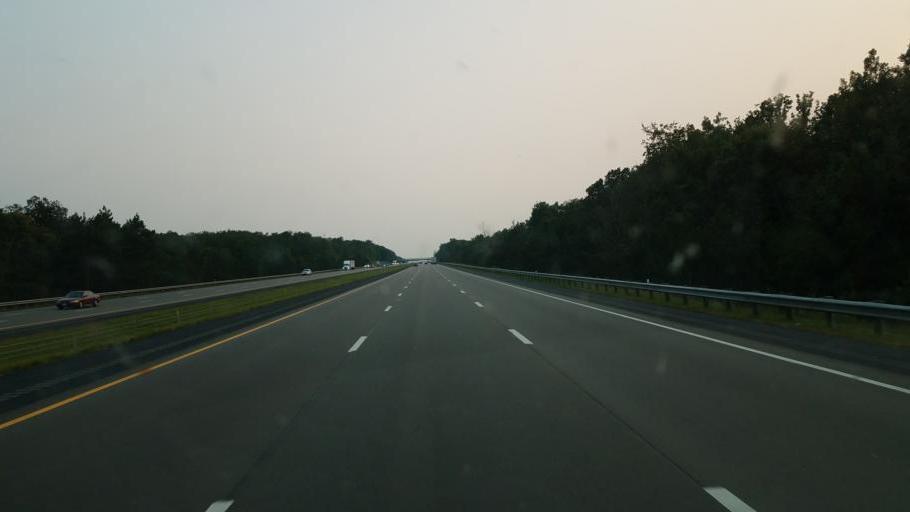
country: US
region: Ohio
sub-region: Medina County
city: Medina
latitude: 41.1054
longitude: -81.8177
